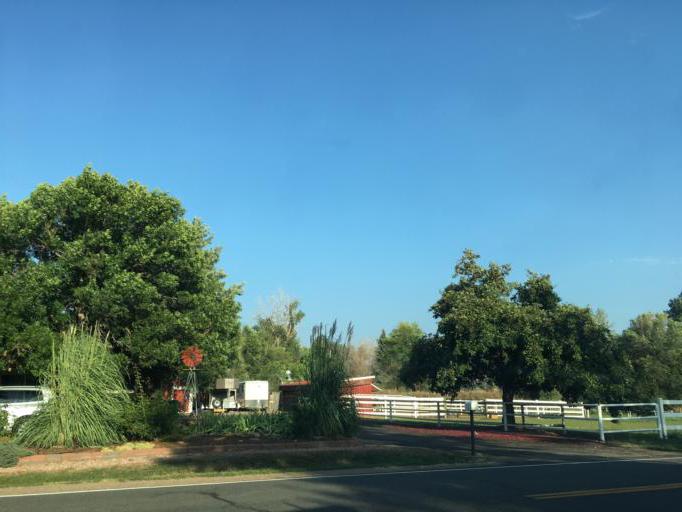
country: US
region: Colorado
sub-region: Jefferson County
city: Applewood
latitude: 39.7930
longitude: -105.1654
